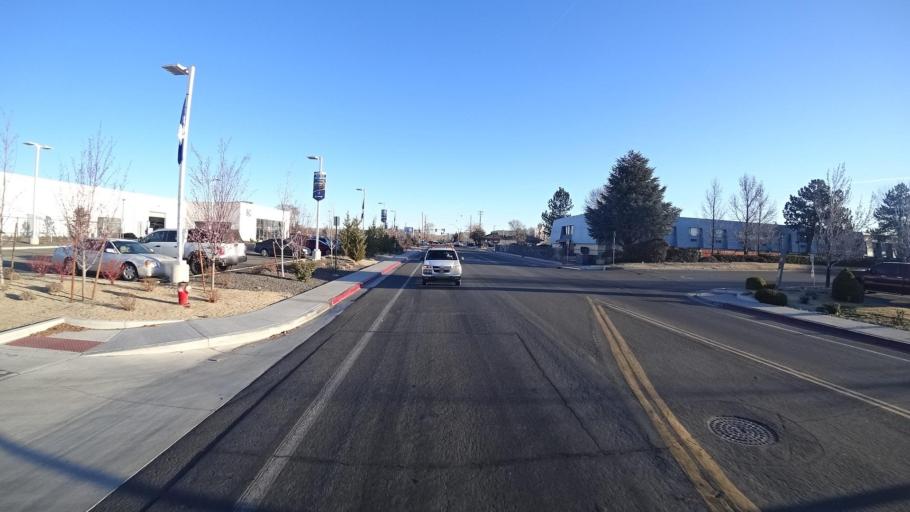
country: US
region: Nevada
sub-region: Washoe County
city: Reno
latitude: 39.5043
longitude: -119.7859
